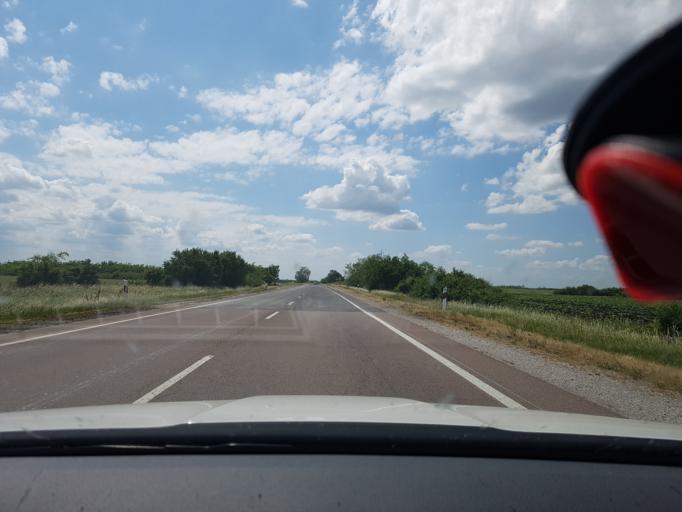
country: HU
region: Heves
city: Kompolt
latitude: 47.7591
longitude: 20.1919
